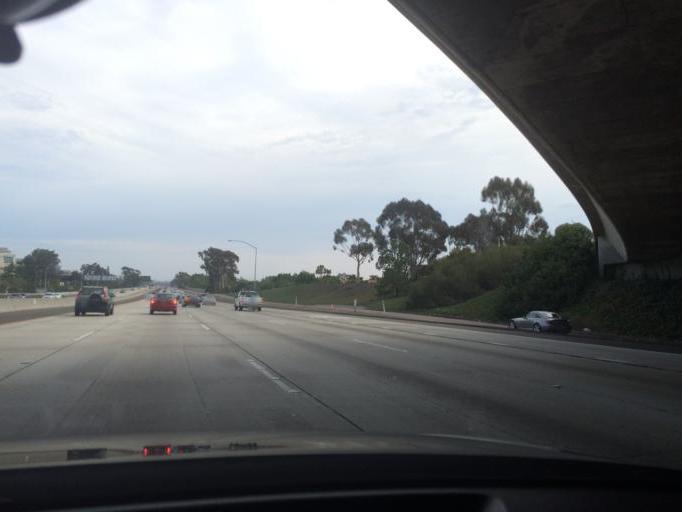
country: US
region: California
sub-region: San Diego County
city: San Diego
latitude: 32.8020
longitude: -117.1554
